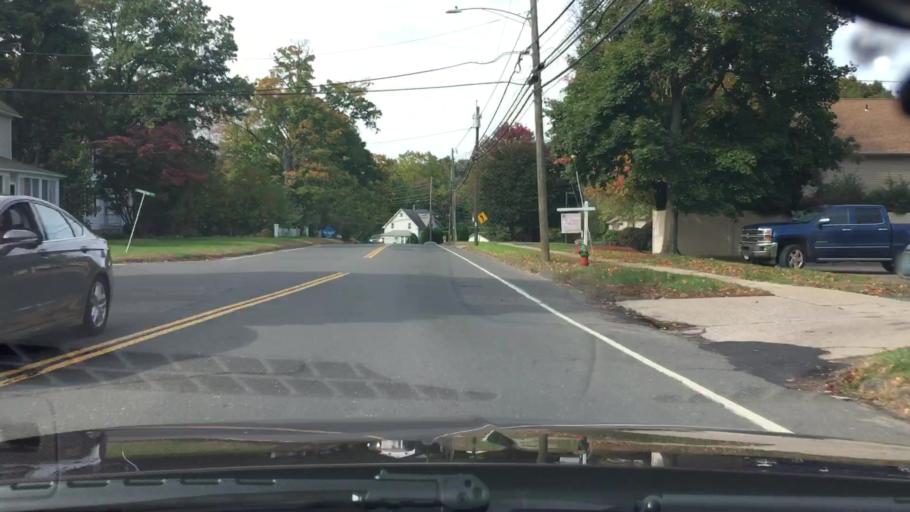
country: US
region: Connecticut
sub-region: Hartford County
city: Bristol
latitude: 41.6768
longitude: -72.9045
